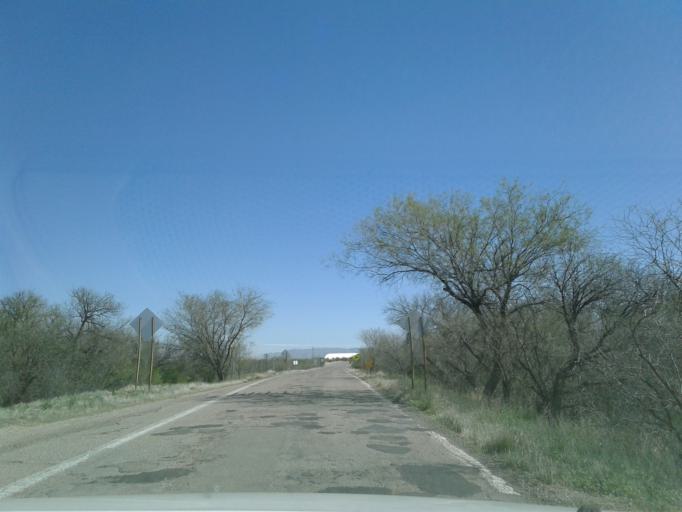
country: US
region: Arizona
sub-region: Pima County
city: Avra Valley
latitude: 32.4667
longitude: -111.3378
